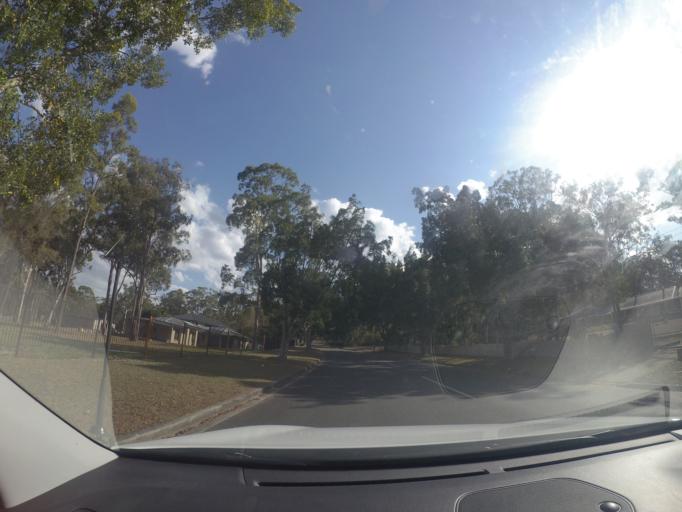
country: AU
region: Queensland
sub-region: Logan
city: Woodridge
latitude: -27.6512
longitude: 153.0645
